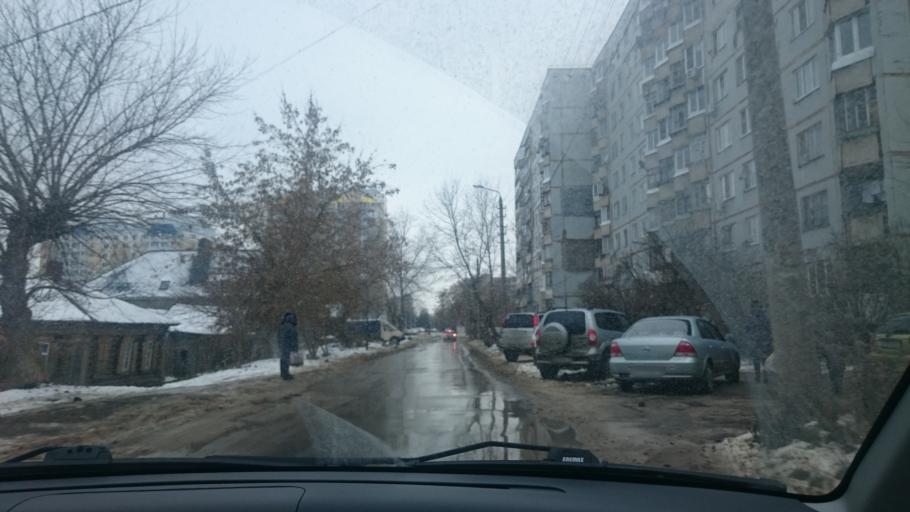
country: RU
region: Tula
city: Tula
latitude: 54.2130
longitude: 37.6075
